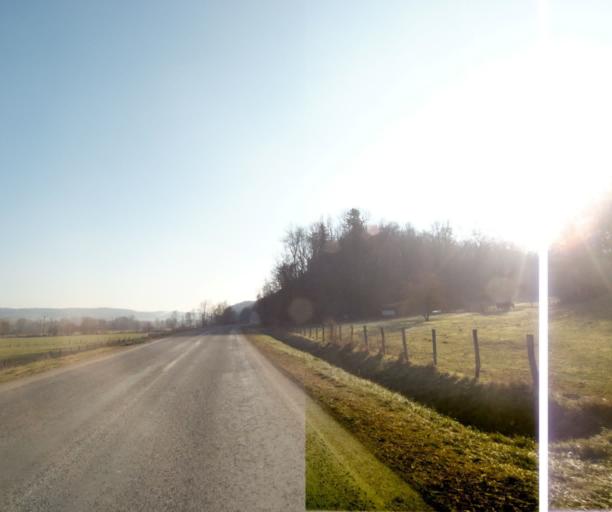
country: FR
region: Champagne-Ardenne
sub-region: Departement de la Haute-Marne
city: Chevillon
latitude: 48.5014
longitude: 5.1178
